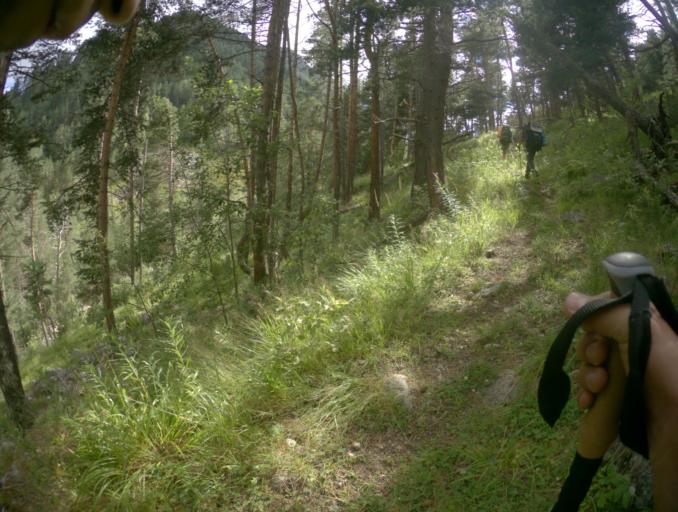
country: RU
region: Karachayevo-Cherkesiya
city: Uchkulan
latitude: 43.3458
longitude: 42.1489
